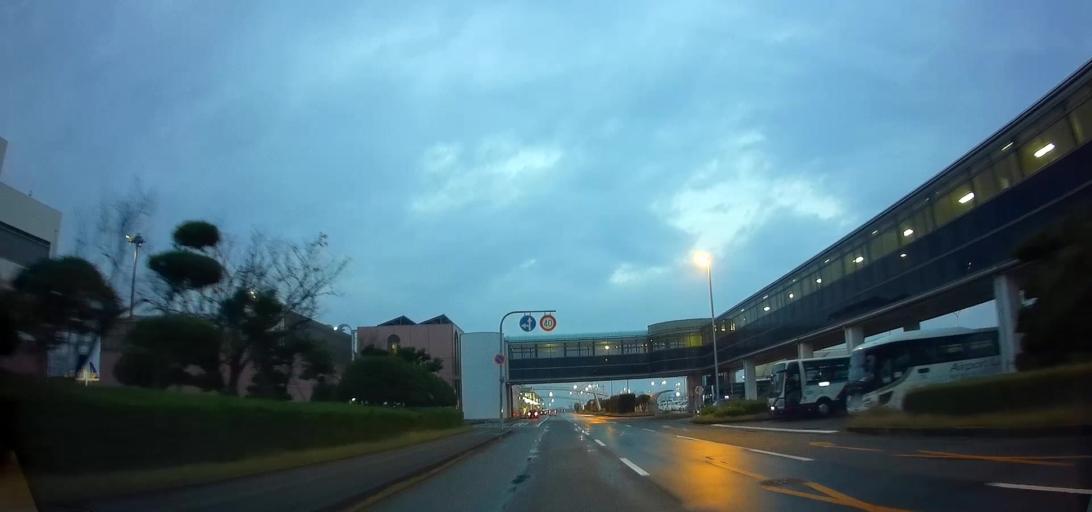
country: JP
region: Nagasaki
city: Omura
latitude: 32.9130
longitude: 129.9242
